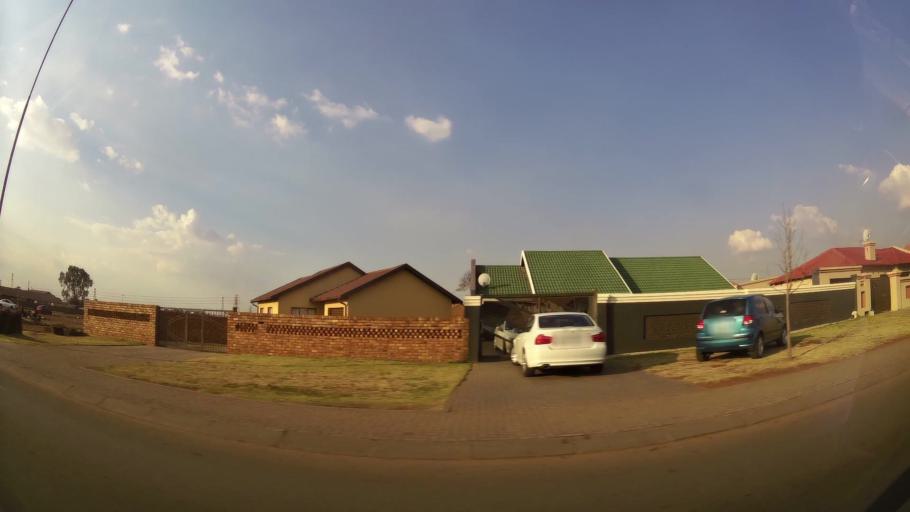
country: ZA
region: Gauteng
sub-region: Ekurhuleni Metropolitan Municipality
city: Germiston
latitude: -26.3467
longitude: 28.2183
